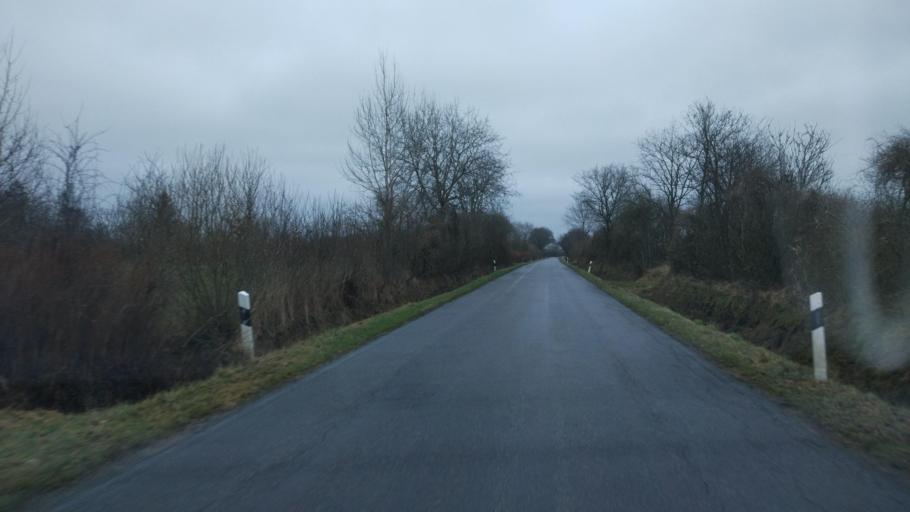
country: DE
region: Schleswig-Holstein
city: Ellingstedt
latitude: 54.4830
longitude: 9.3935
